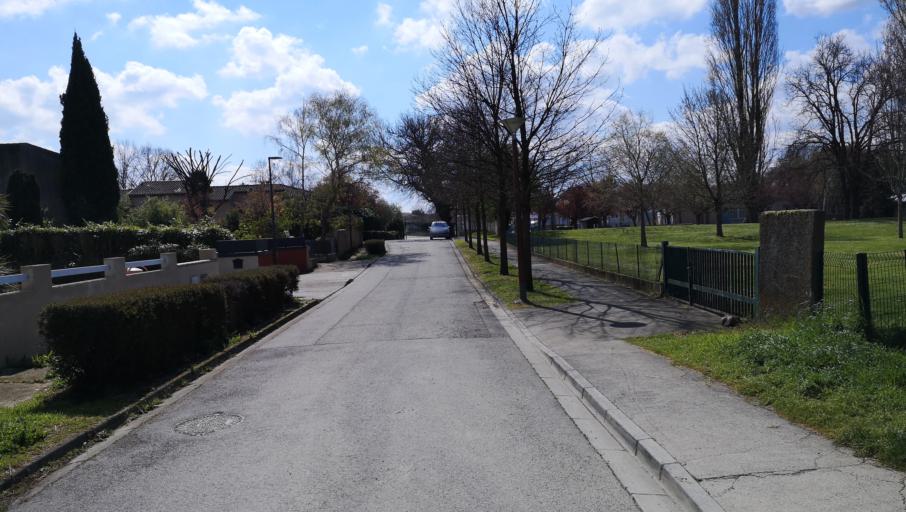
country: FR
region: Midi-Pyrenees
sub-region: Departement de la Haute-Garonne
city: Blagnac
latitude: 43.6444
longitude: 1.3931
